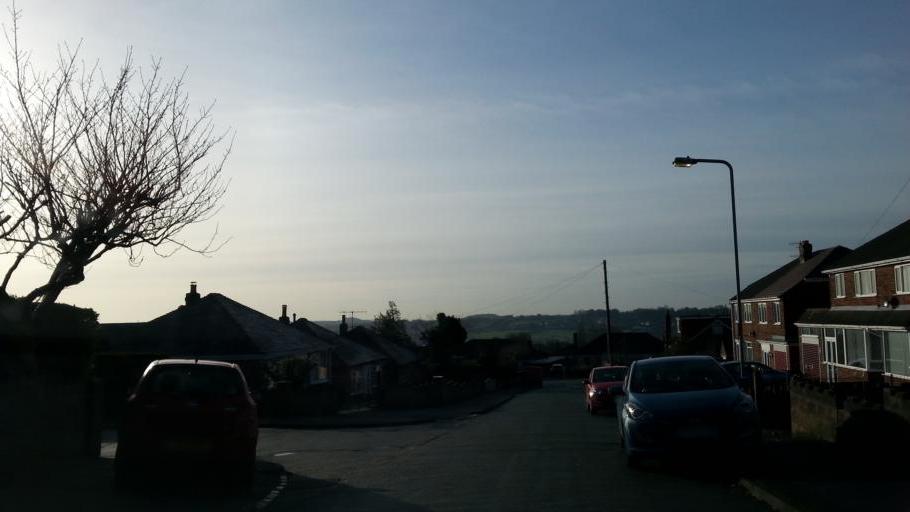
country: GB
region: England
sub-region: Staffordshire
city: Biddulph
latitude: 53.0737
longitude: -2.1387
